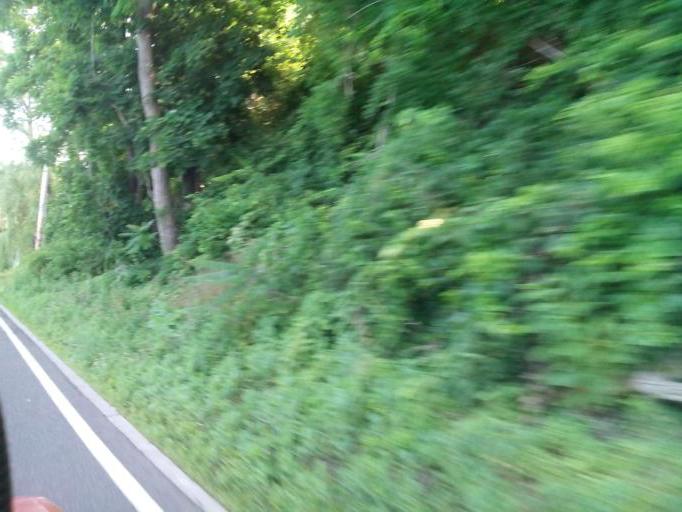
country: US
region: New York
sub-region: Nassau County
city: Oyster Bay
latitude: 40.8853
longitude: -73.5482
